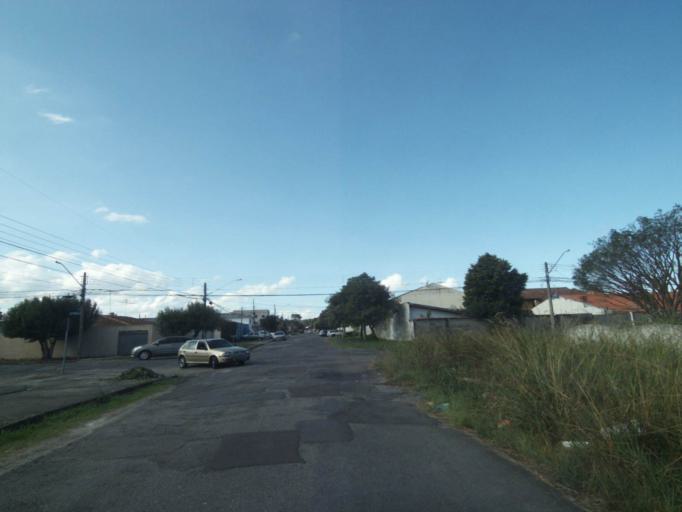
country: BR
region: Parana
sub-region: Pinhais
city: Pinhais
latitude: -25.4392
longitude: -49.2102
